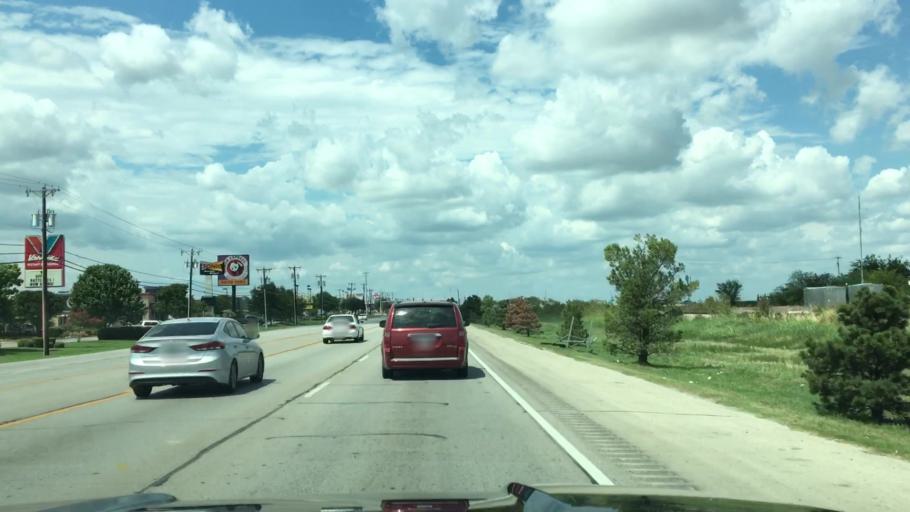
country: US
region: Texas
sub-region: Tarrant County
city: Saginaw
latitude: 32.8779
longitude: -97.3791
